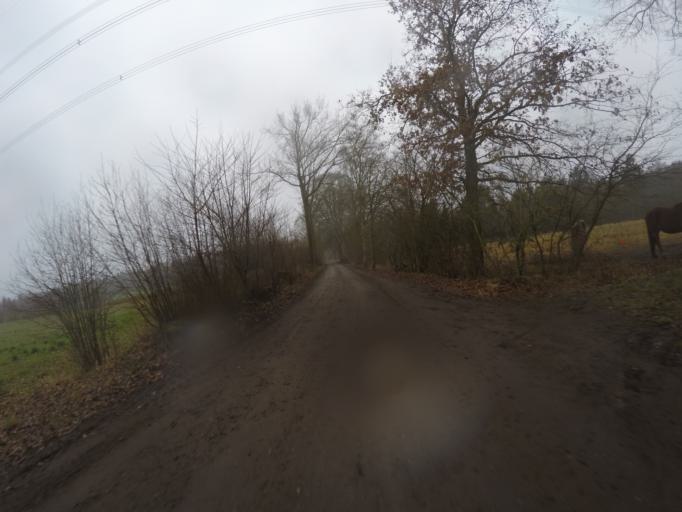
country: DE
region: Schleswig-Holstein
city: Ellerau
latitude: 53.7409
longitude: 9.9243
